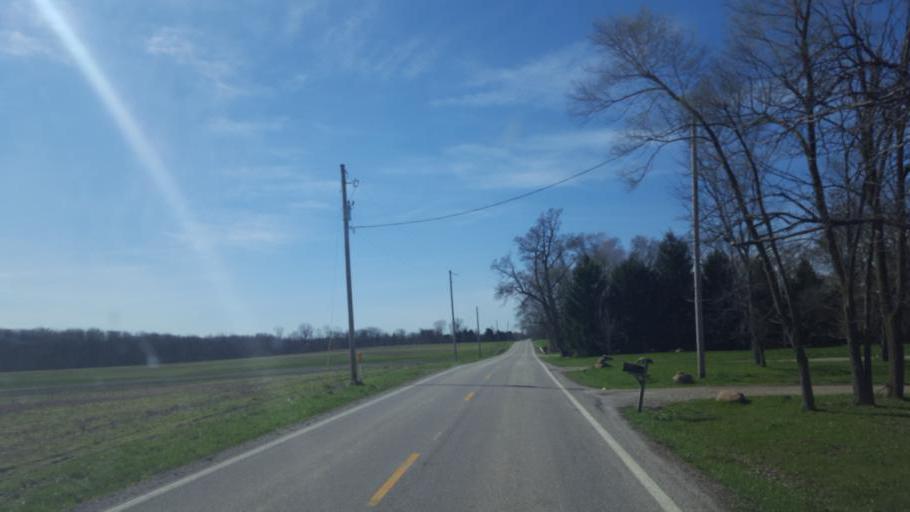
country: US
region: Ohio
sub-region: Delaware County
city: Ashley
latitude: 40.4774
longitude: -82.9634
